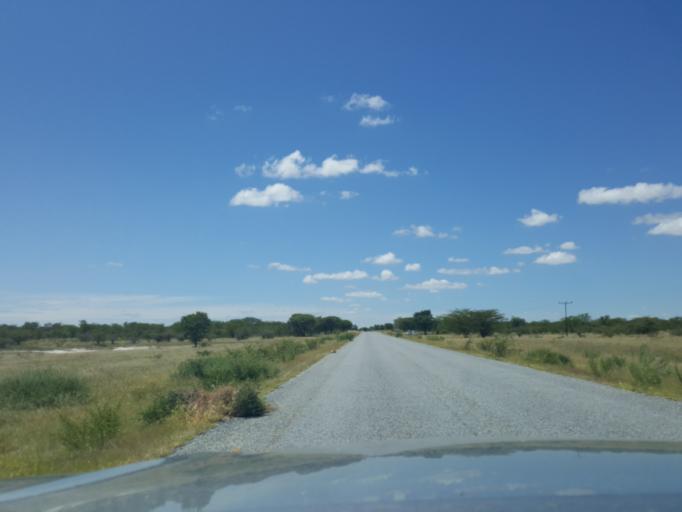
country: BW
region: Central
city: Nata
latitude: -20.1465
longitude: 25.7267
